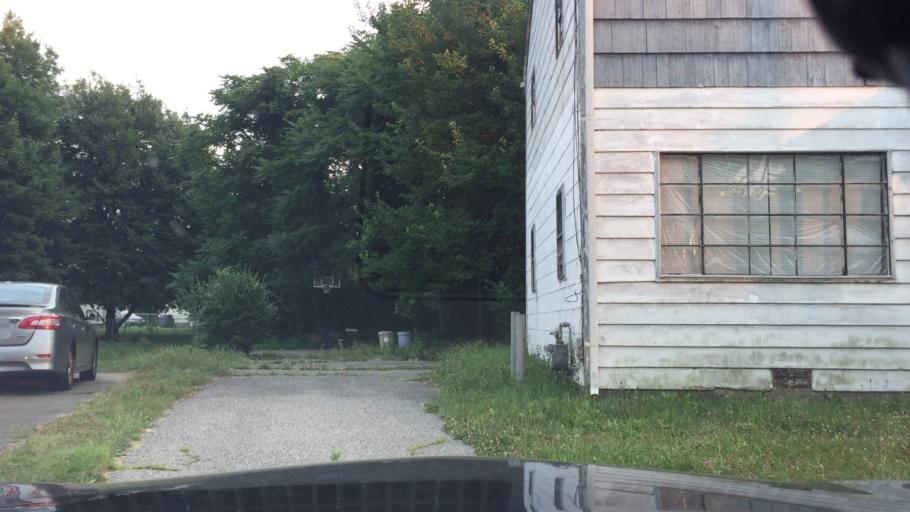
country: US
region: Connecticut
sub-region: Fairfield County
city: Stratford
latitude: 41.1731
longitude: -73.1375
